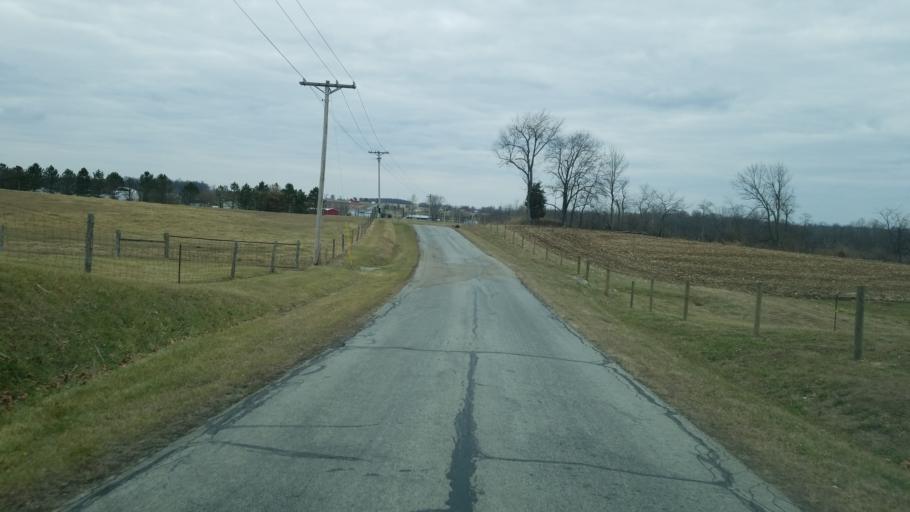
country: US
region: Ohio
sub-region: Highland County
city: Hillsboro
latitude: 39.2199
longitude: -83.4858
